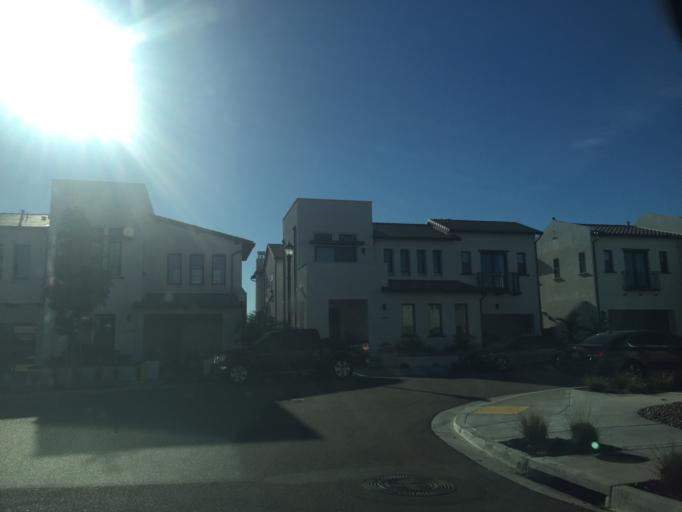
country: US
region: California
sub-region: San Diego County
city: Fairbanks Ranch
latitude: 32.9680
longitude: -117.1937
